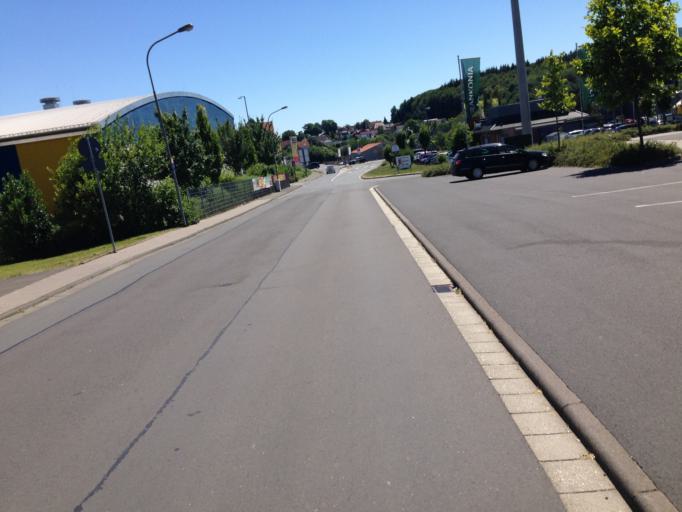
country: DE
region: Hesse
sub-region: Regierungsbezirk Giessen
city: Reiskirchen
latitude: 50.5991
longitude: 8.8221
